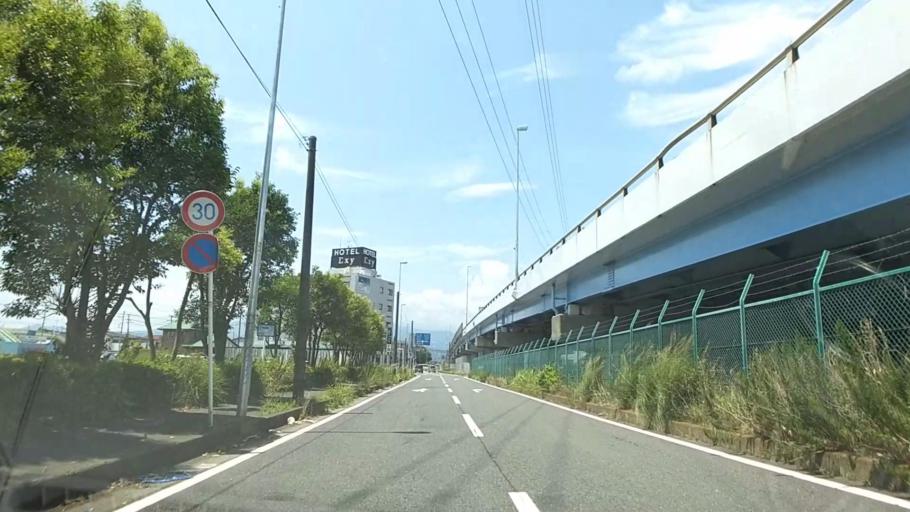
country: JP
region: Kanagawa
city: Zama
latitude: 35.4637
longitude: 139.3904
